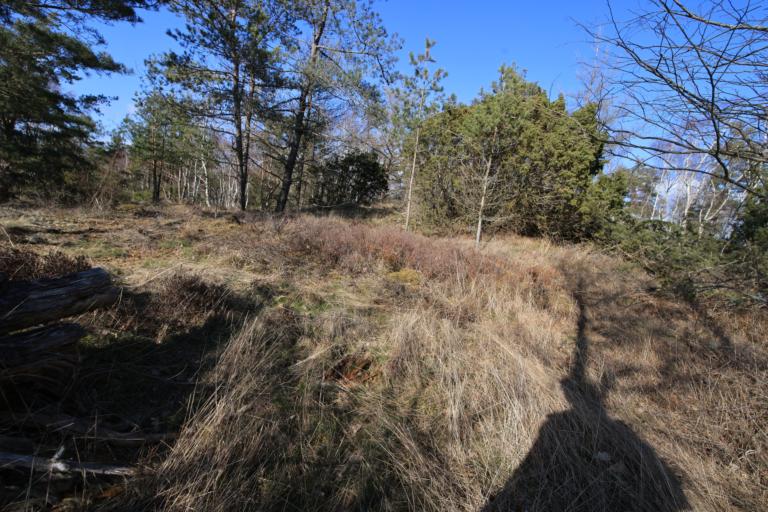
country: SE
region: Halland
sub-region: Varbergs Kommun
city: Varberg
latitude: 57.1669
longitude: 12.2598
